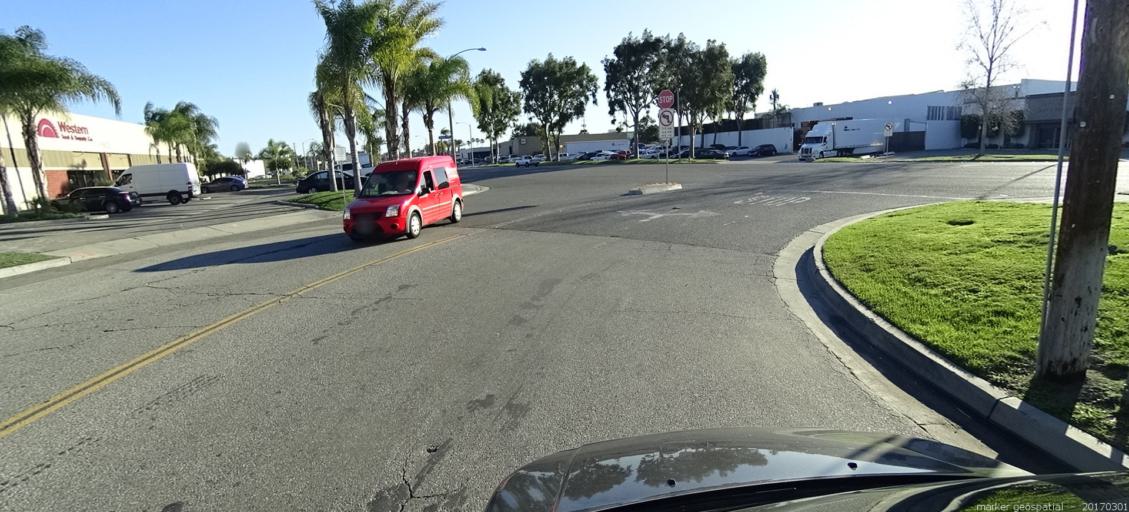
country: US
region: California
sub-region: Orange County
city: Placentia
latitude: 33.8585
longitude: -117.8373
